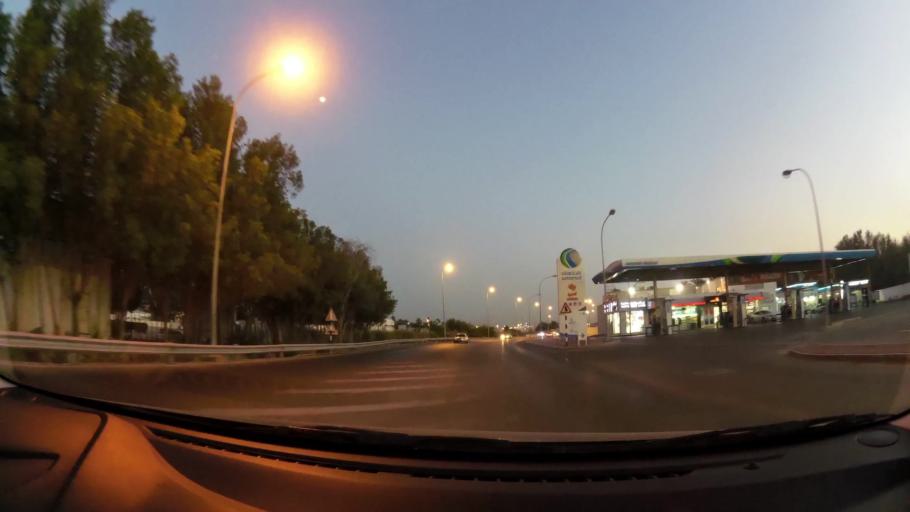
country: OM
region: Muhafazat Masqat
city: As Sib al Jadidah
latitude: 23.6744
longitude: 58.1920
